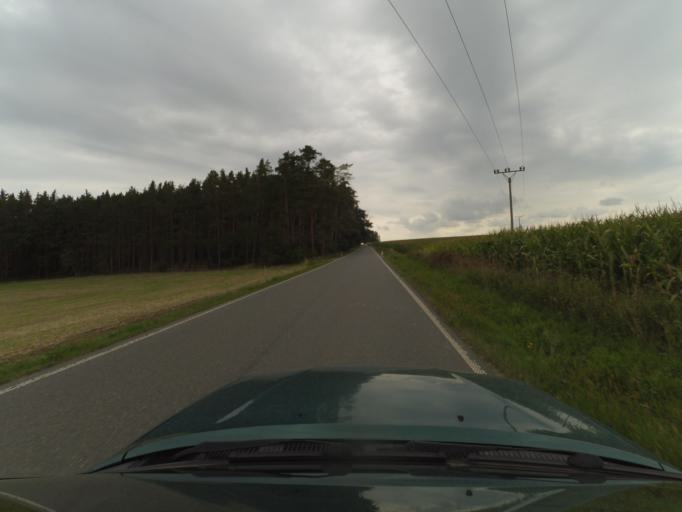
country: CZ
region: Plzensky
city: Hromnice
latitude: 49.8389
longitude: 13.4831
